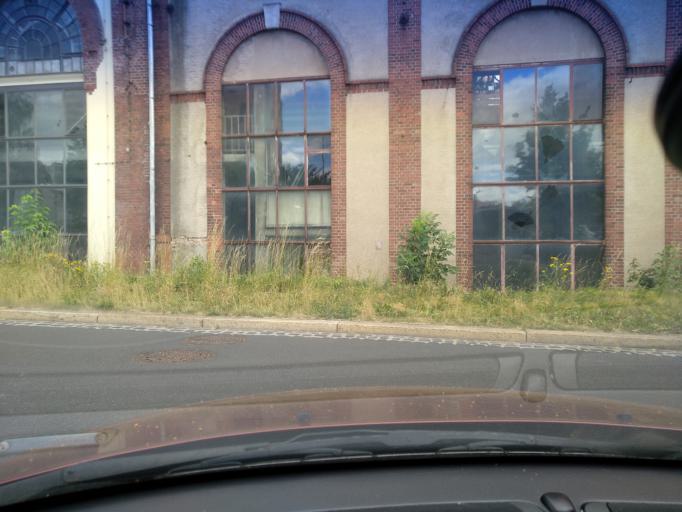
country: DE
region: Saxony
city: Goerlitz
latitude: 51.1413
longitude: 14.9768
